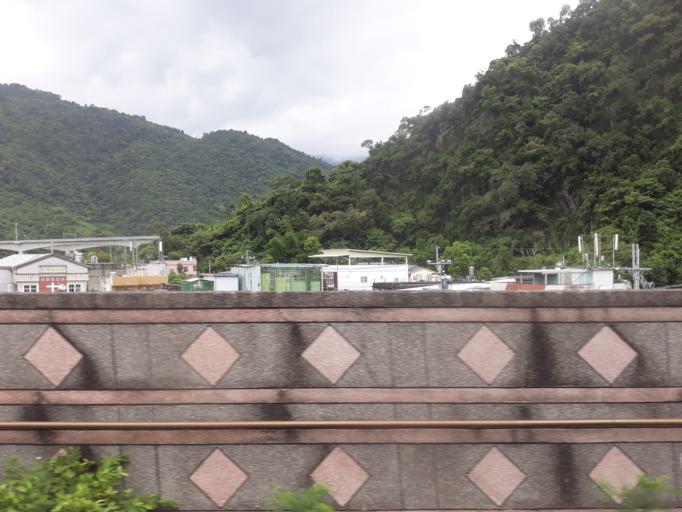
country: TW
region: Taiwan
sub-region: Yilan
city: Yilan
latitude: 24.4446
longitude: 121.7776
